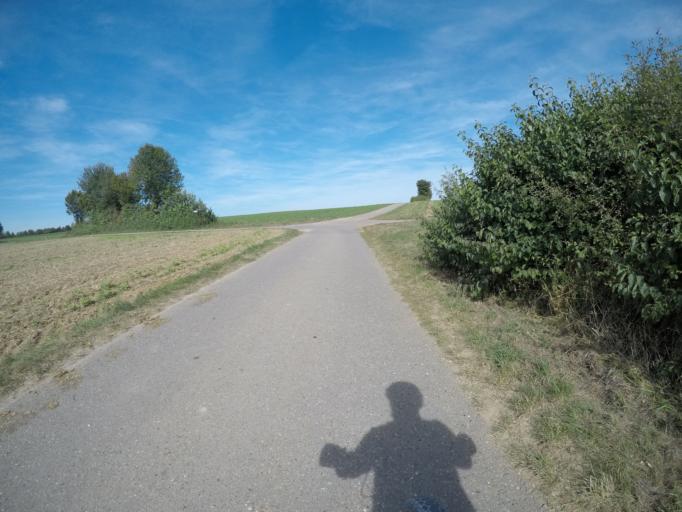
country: DE
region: Baden-Wuerttemberg
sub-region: Regierungsbezirk Stuttgart
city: Oberriexingen
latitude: 48.9427
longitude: 9.0283
